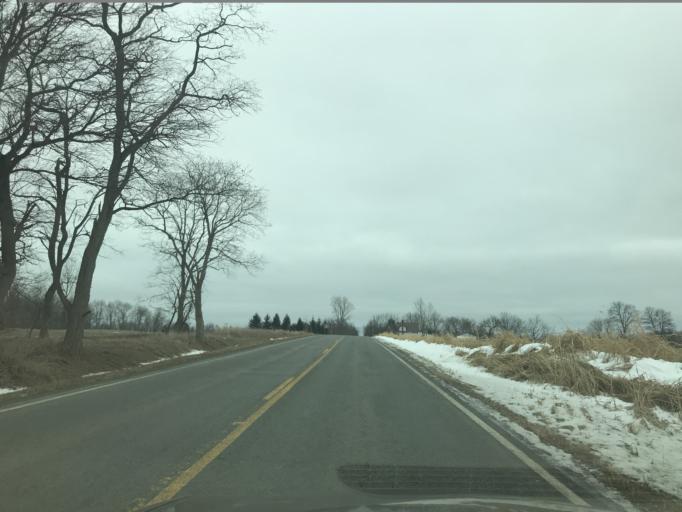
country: US
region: Michigan
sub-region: Jackson County
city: Brooklyn
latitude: 42.0734
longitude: -84.3435
